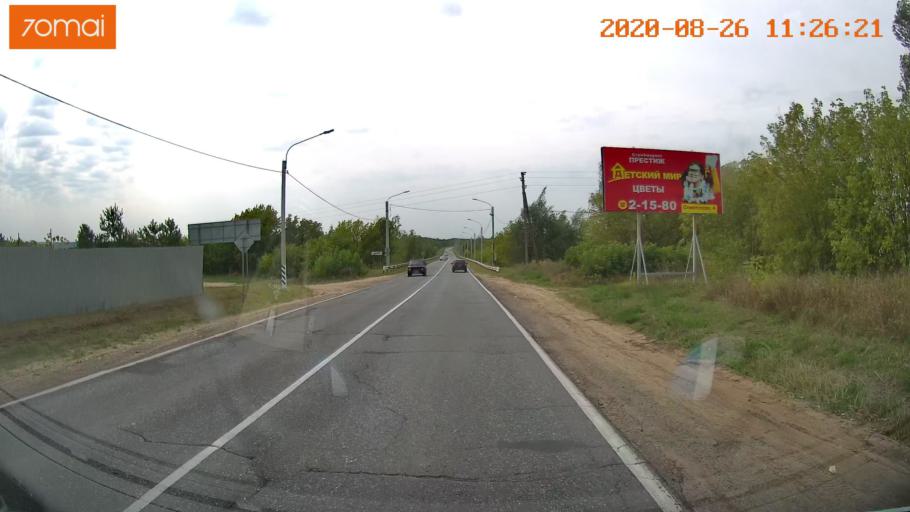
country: RU
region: Rjazan
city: Shilovo
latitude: 54.3345
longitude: 40.9516
